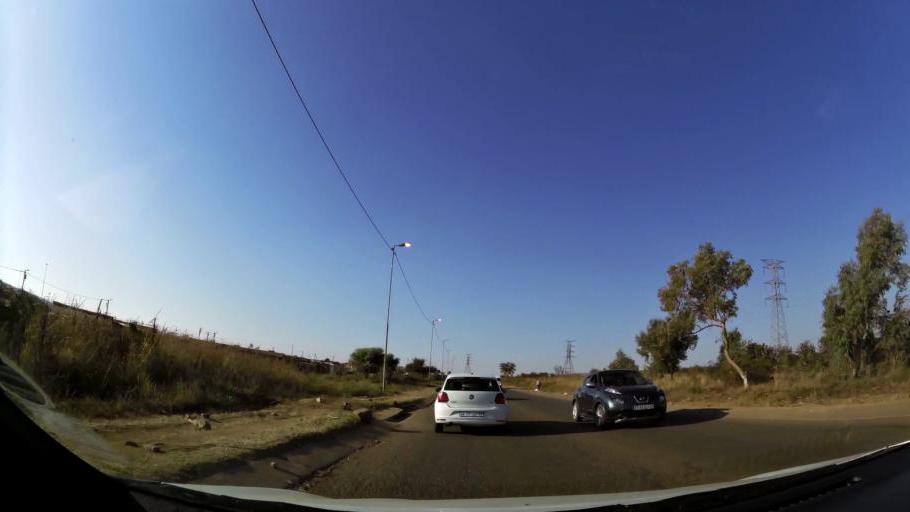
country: ZA
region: Gauteng
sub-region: City of Tshwane Metropolitan Municipality
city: Cullinan
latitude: -25.7344
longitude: 28.3961
